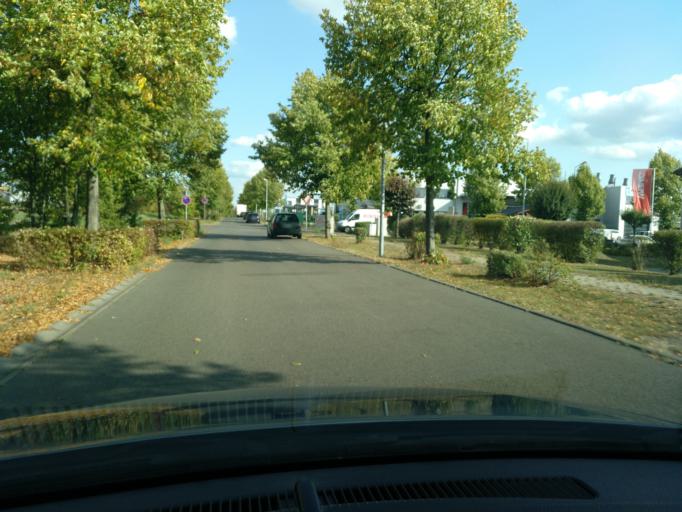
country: DE
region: Berlin
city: Mahlsdorf
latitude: 52.5069
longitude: 13.6347
